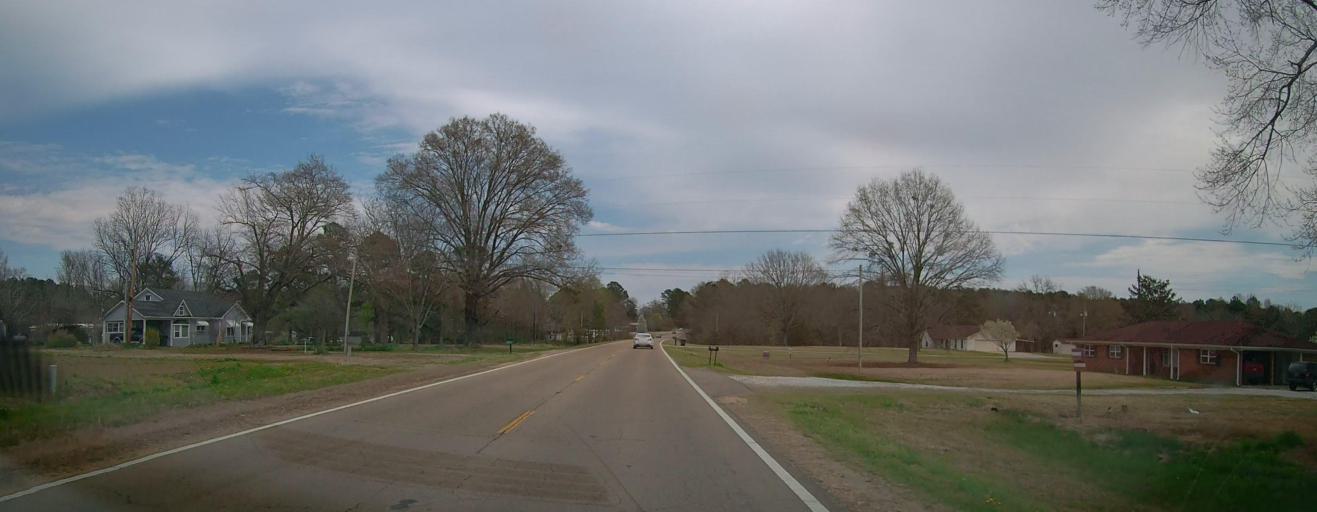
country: US
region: Mississippi
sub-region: Itawamba County
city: Mantachie
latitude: 34.2669
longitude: -88.5576
